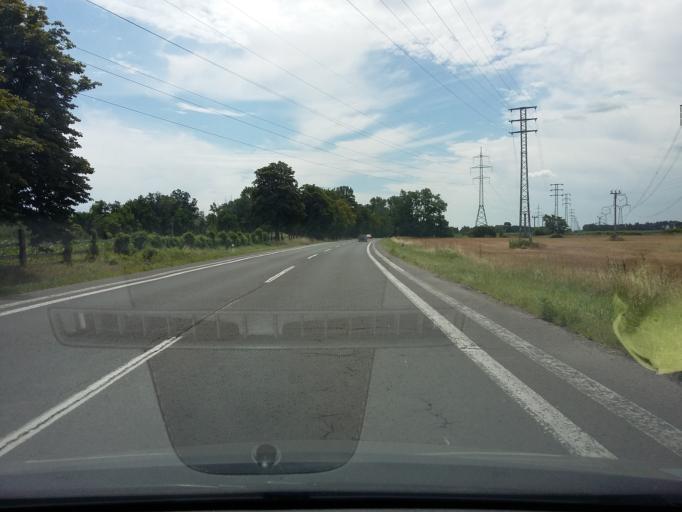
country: SK
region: Bratislavsky
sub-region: Okres Malacky
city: Malacky
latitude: 48.4823
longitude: 17.0134
